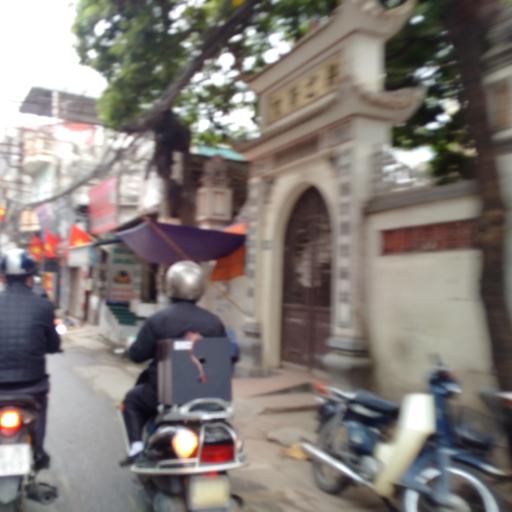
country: VN
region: Ha Noi
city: Cau Dien
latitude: 21.0592
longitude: 105.7828
